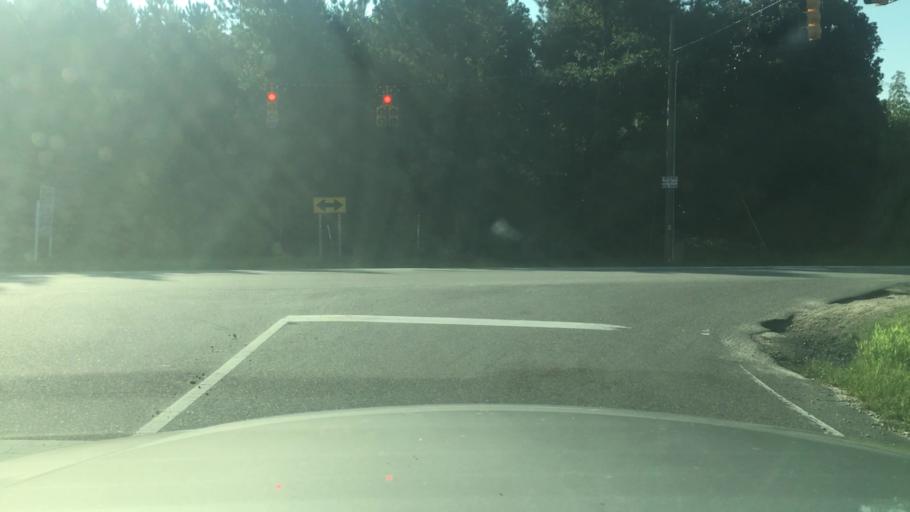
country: US
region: North Carolina
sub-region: Harnett County
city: Walkertown
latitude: 35.2054
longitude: -78.8492
